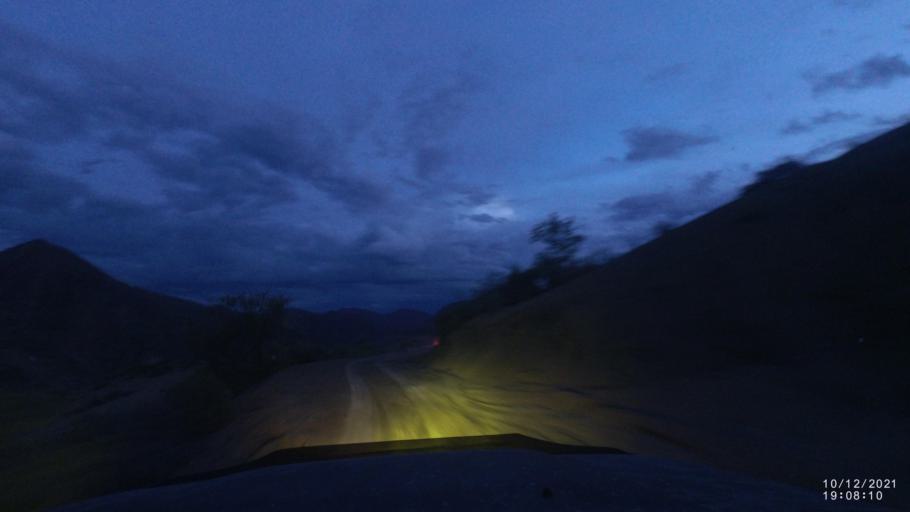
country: BO
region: Cochabamba
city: Tarata
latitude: -17.9098
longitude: -65.9375
